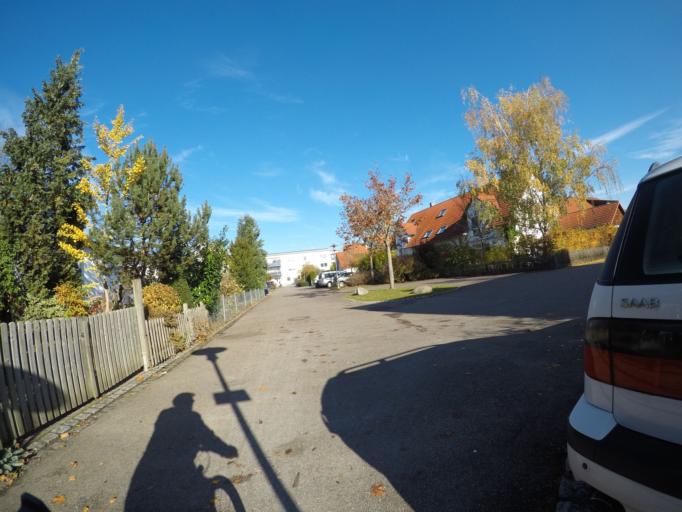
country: DE
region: Bavaria
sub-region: Swabia
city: Neu-Ulm
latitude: 48.4092
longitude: 10.0291
